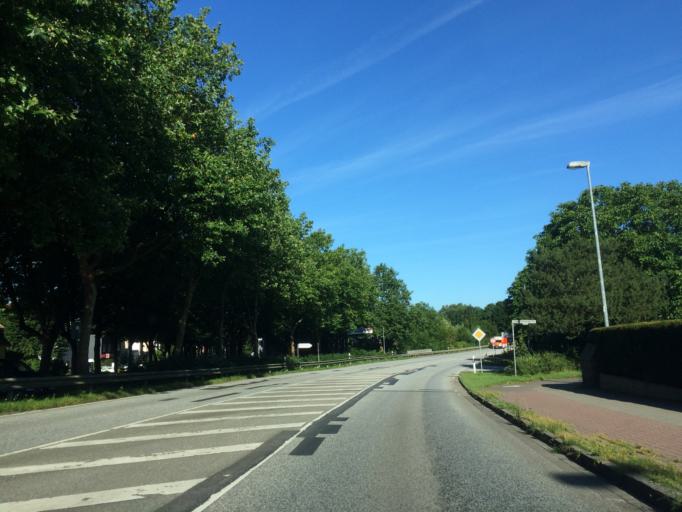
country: DE
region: Schleswig-Holstein
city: Ploen
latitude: 54.1591
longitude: 10.4339
